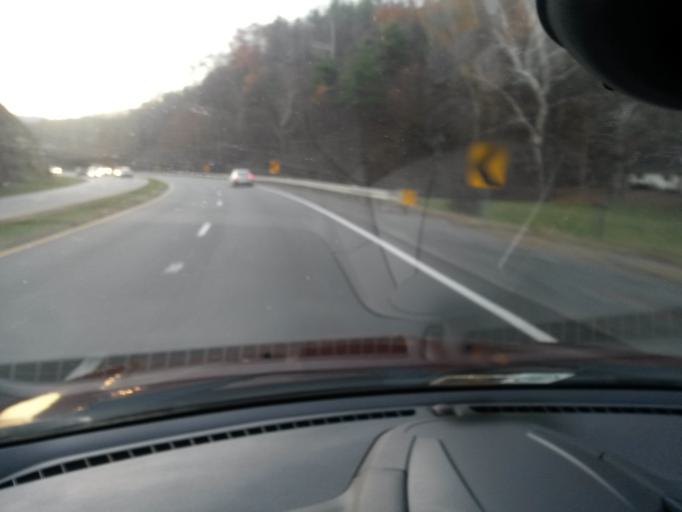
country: US
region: Virginia
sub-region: Roanoke County
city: Narrows
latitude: 37.1950
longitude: -79.9422
